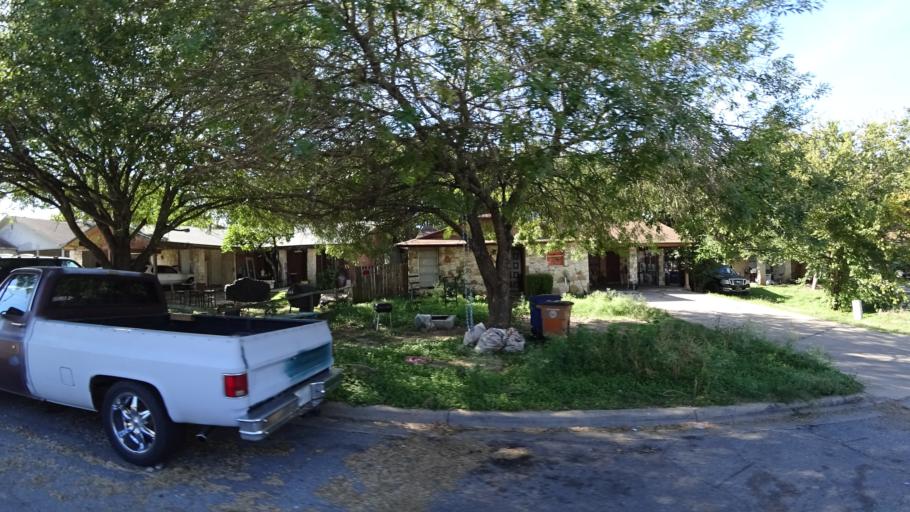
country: US
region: Texas
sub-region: Travis County
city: Austin
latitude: 30.1943
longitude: -97.7393
